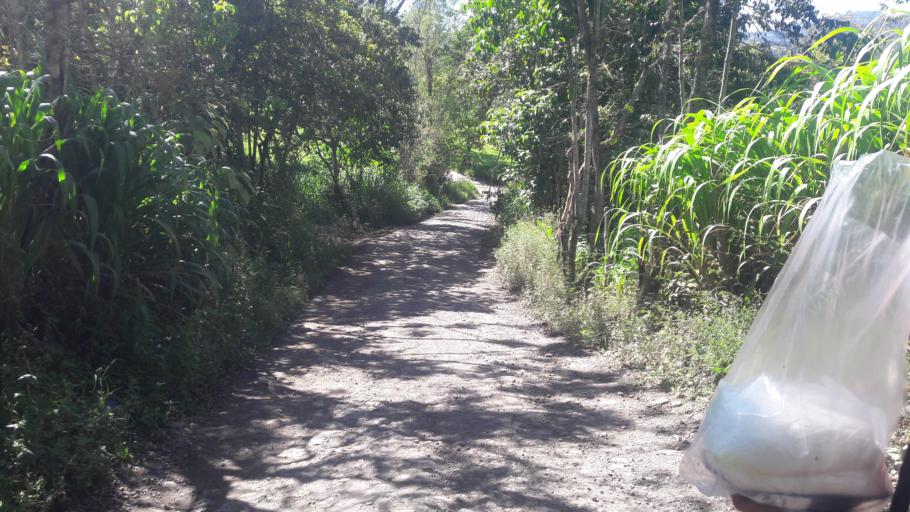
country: CO
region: Cundinamarca
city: Tenza
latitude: 5.0875
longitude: -73.4229
